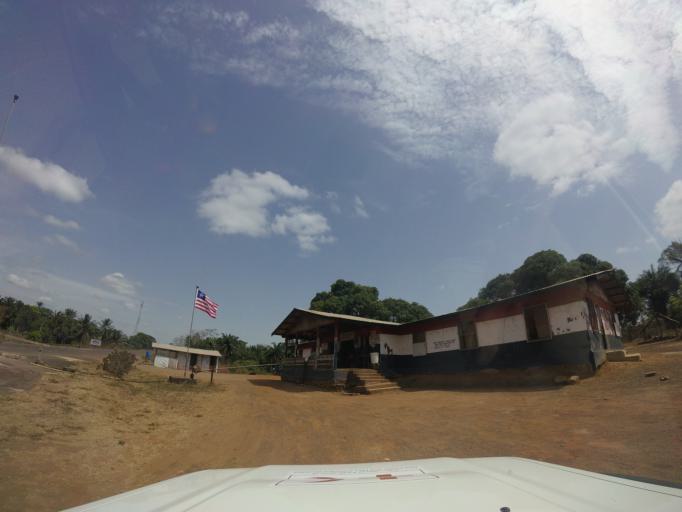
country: LR
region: Grand Cape Mount
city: Robertsport
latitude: 6.9652
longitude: -11.3108
